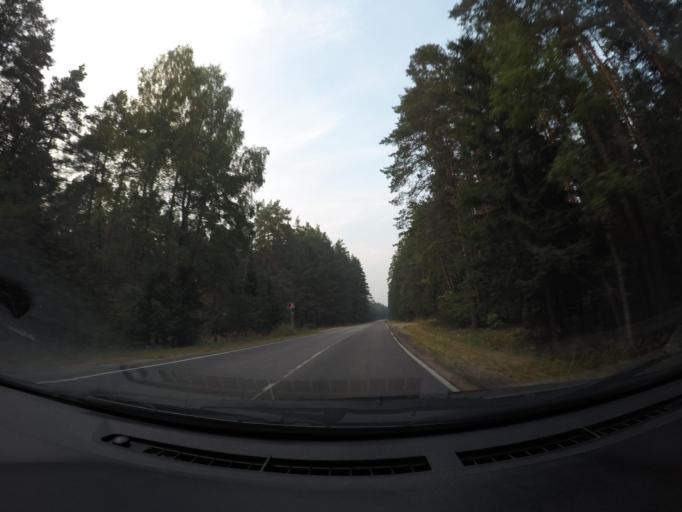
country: RU
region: Moskovskaya
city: Imeni Tsyurupy
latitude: 55.5065
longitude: 38.7151
